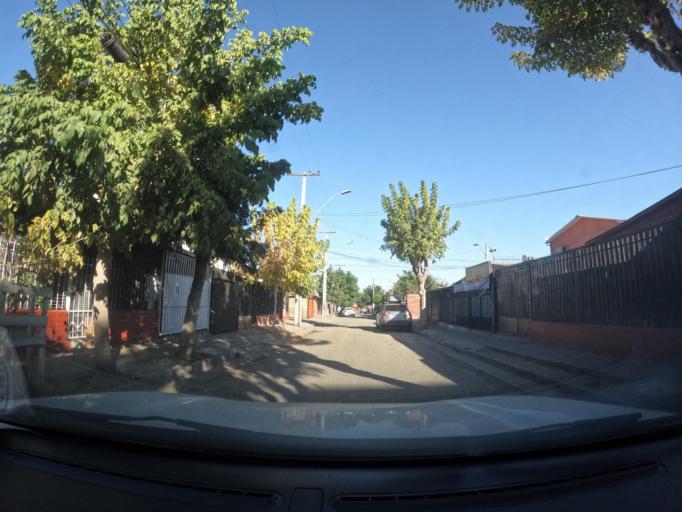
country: CL
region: Santiago Metropolitan
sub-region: Provincia de Santiago
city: Villa Presidente Frei, Nunoa, Santiago, Chile
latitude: -33.5019
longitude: -70.5682
